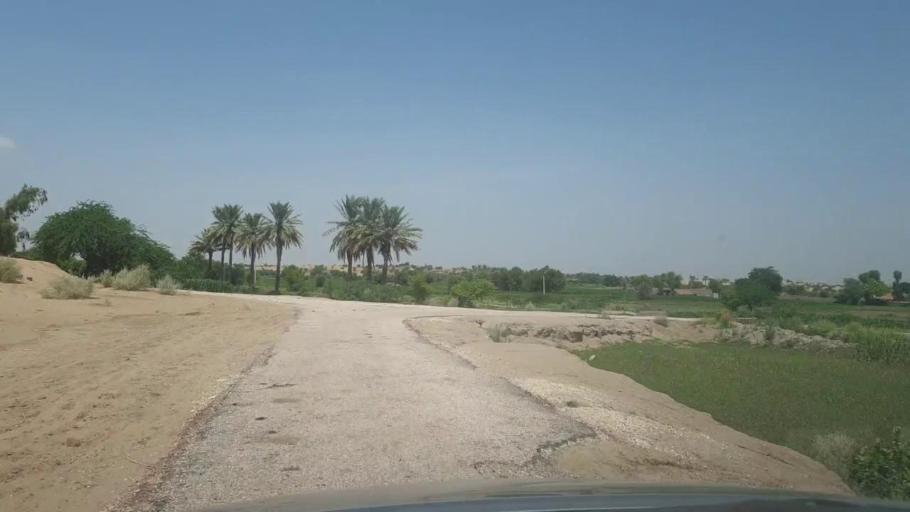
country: PK
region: Sindh
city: Kot Diji
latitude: 27.3207
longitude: 69.0192
